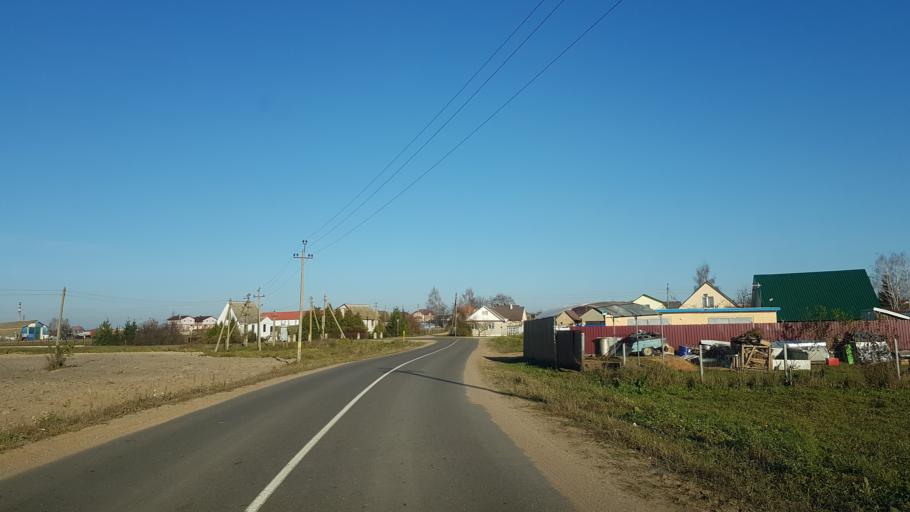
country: BY
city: Fanipol
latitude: 53.7202
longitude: 27.3126
